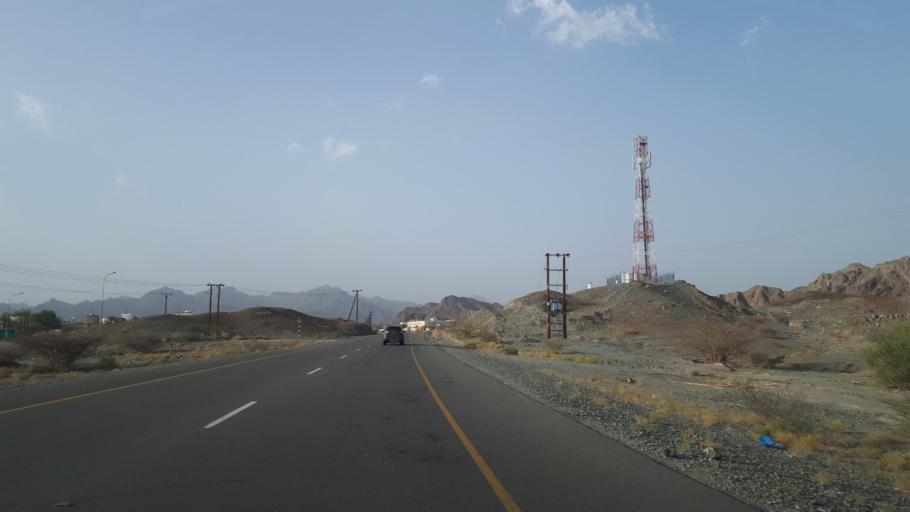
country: OM
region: Az Zahirah
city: Yanqul
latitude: 23.4598
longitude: 56.7944
